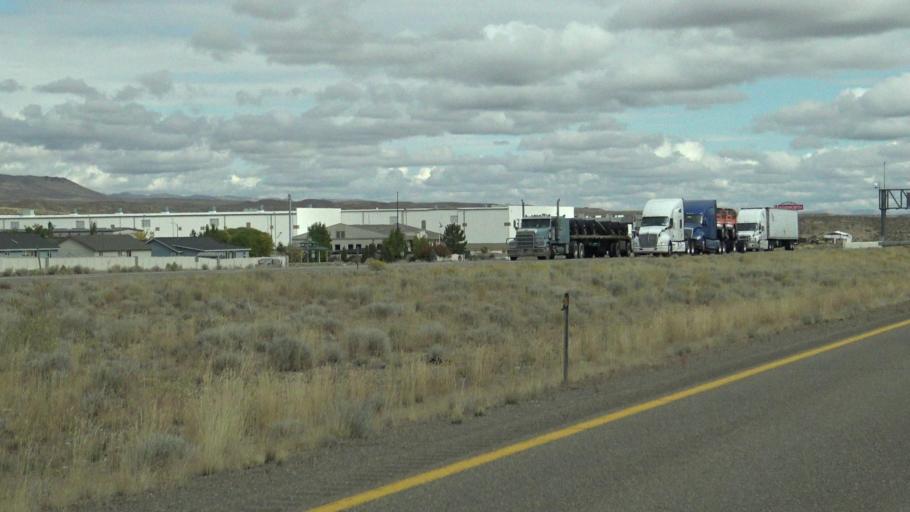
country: US
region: Nevada
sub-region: Elko County
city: Elko
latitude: 40.8629
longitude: -115.7356
